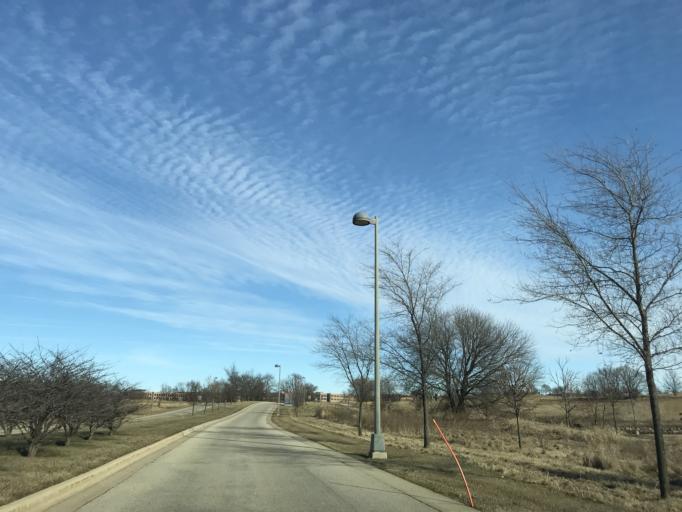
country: US
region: Wisconsin
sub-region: Dane County
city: Windsor
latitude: 43.1537
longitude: -89.2981
